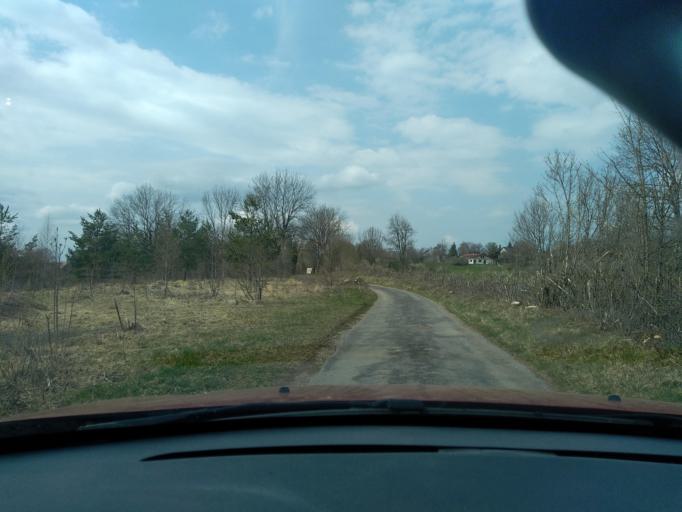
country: FR
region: Franche-Comte
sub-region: Departement du Jura
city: Moirans-en-Montagne
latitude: 46.4537
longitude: 5.7348
